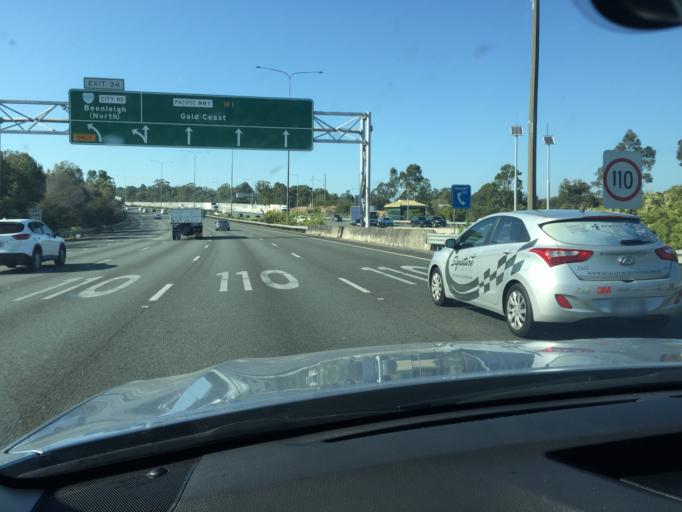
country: AU
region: Queensland
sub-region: Logan
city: Beenleigh
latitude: -27.6982
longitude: 153.1961
